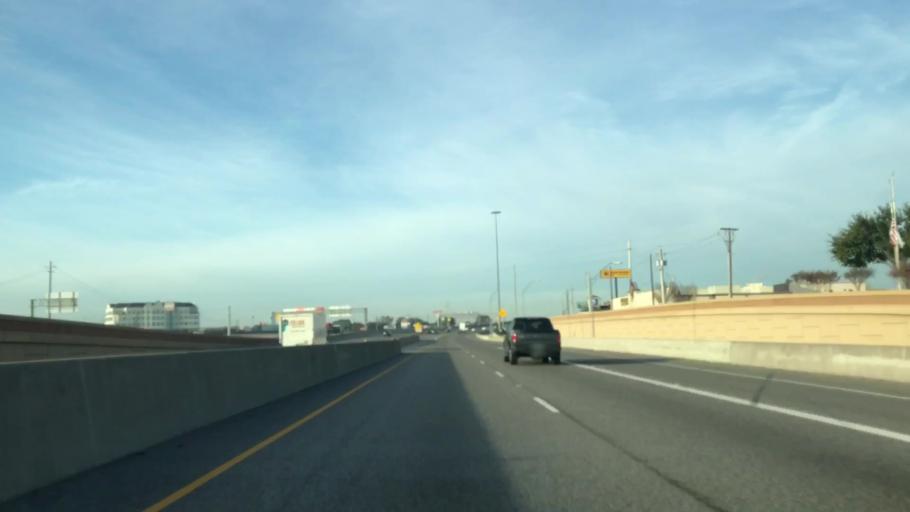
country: US
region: Texas
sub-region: Tarrant County
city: Bedford
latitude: 32.8379
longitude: -97.1248
